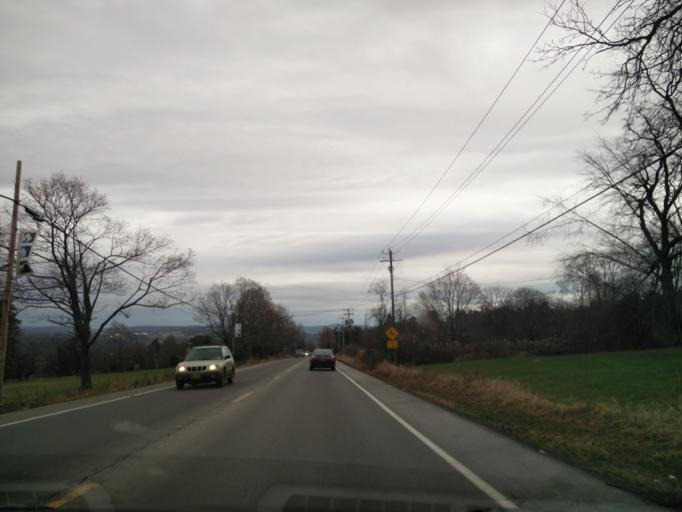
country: US
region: New York
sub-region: Tompkins County
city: Northwest Ithaca
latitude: 42.4651
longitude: -76.5372
